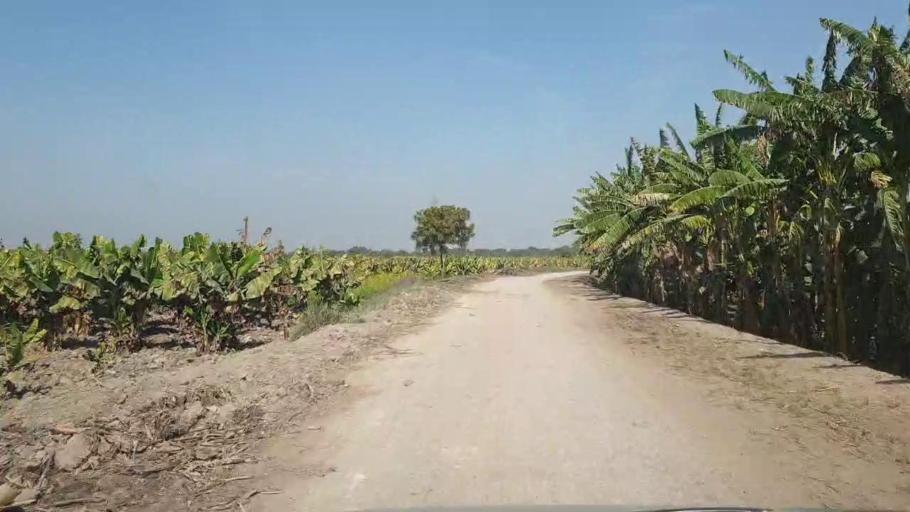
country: PK
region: Sindh
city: Chambar
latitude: 25.3634
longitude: 68.7896
